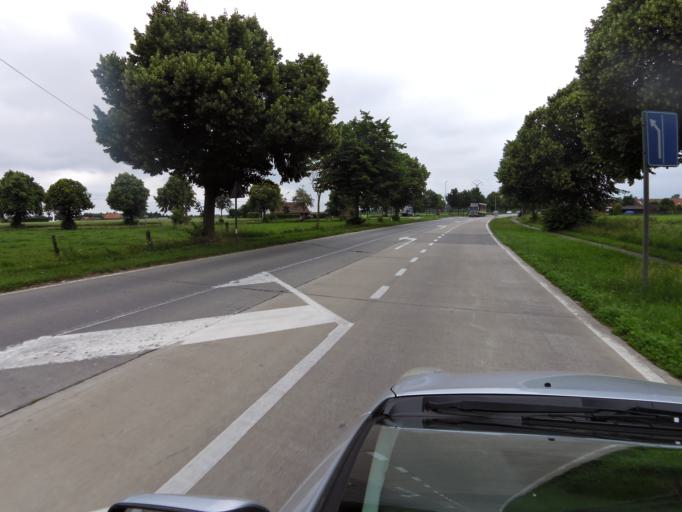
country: BE
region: Flanders
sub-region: Provincie West-Vlaanderen
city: Ieper
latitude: 50.9158
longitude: 2.8393
